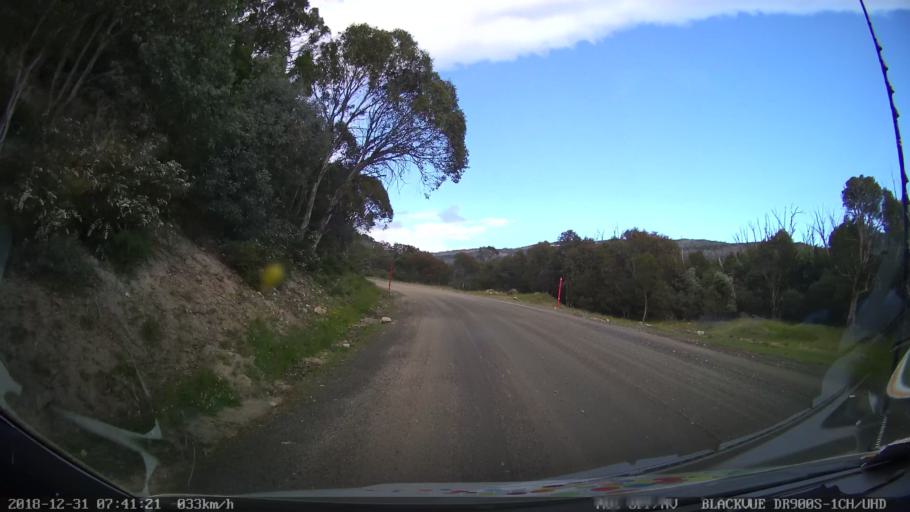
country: AU
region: New South Wales
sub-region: Snowy River
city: Jindabyne
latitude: -36.3529
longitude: 148.4124
